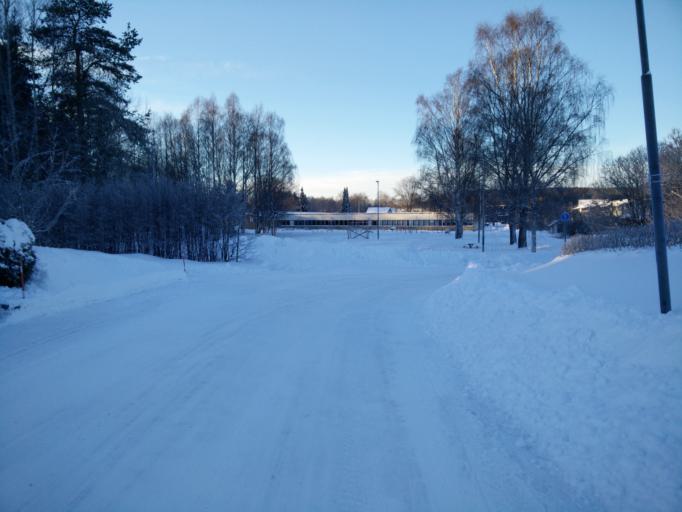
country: SE
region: Vaesternorrland
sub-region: Sundsvalls Kommun
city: Kvissleby
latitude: 62.2940
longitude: 17.3711
